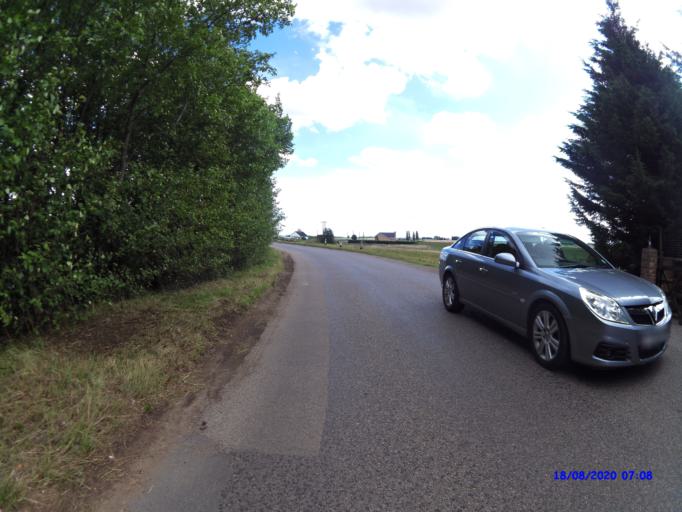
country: GB
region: England
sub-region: Cambridgeshire
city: Whittlesey
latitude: 52.5446
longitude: -0.1127
